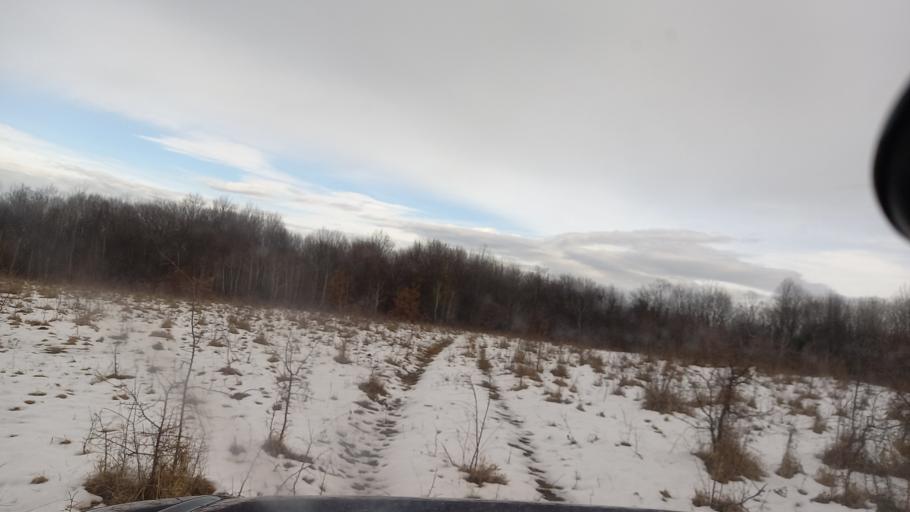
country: RU
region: Adygeya
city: Kamennomostskiy
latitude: 44.2534
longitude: 40.1808
